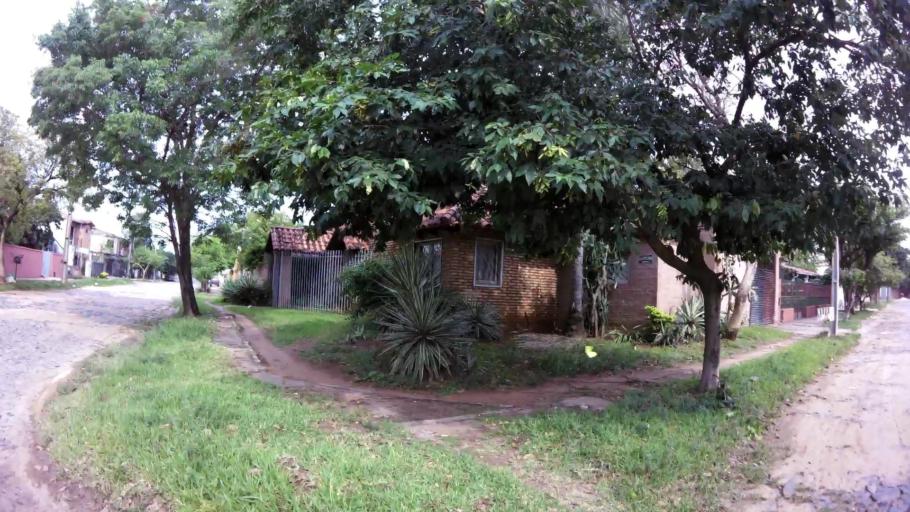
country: PY
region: Central
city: Fernando de la Mora
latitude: -25.3004
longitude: -57.5535
